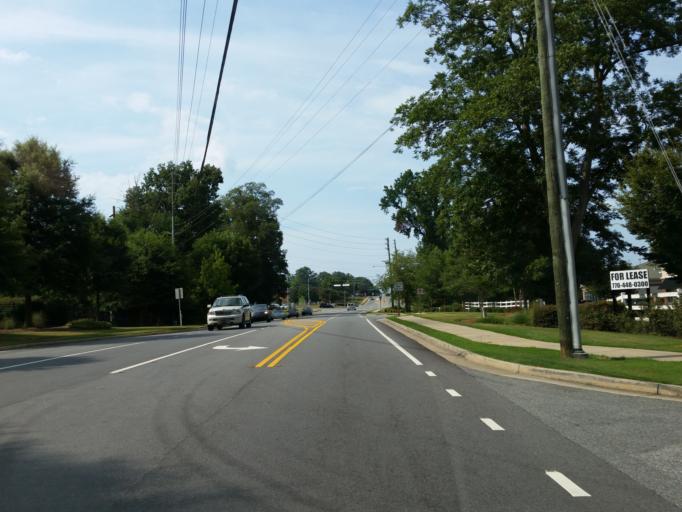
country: US
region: Georgia
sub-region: Fulton County
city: Roswell
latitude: 34.0571
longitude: -84.3834
